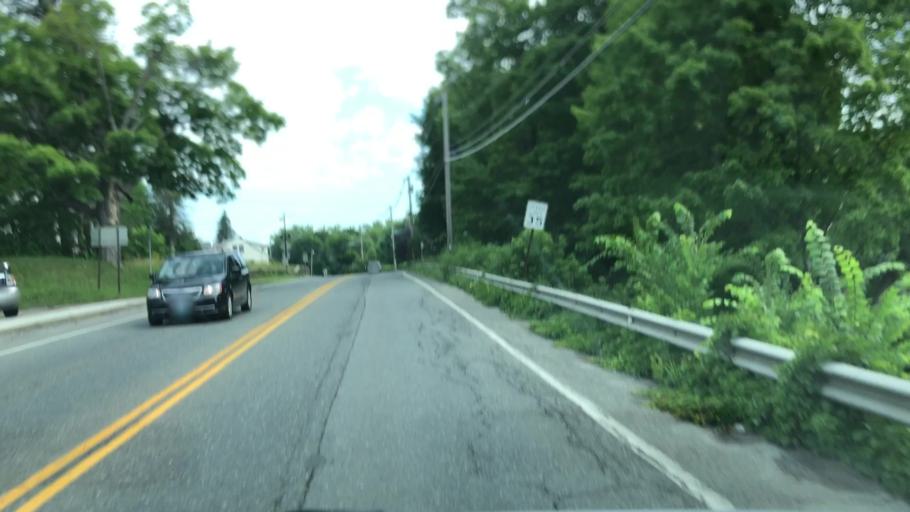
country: US
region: Massachusetts
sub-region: Berkshire County
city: Adams
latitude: 42.6381
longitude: -73.1126
